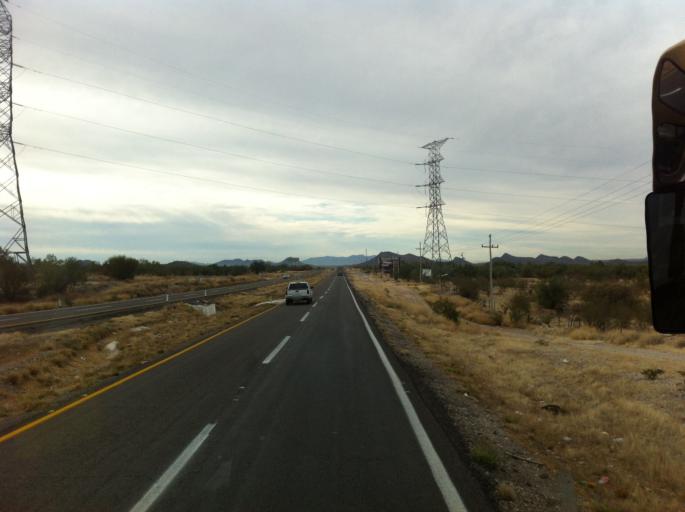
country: MX
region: Sonora
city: Hermosillo
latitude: 28.9707
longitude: -110.9639
